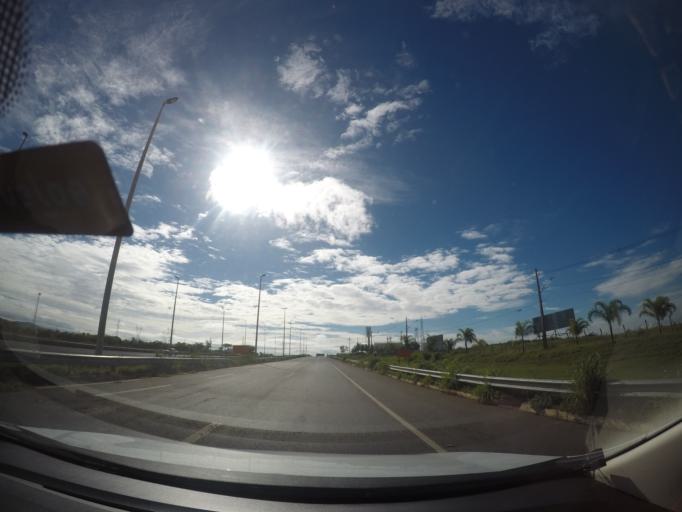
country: BR
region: Goias
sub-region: Senador Canedo
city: Senador Canedo
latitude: -16.6855
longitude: -49.1601
